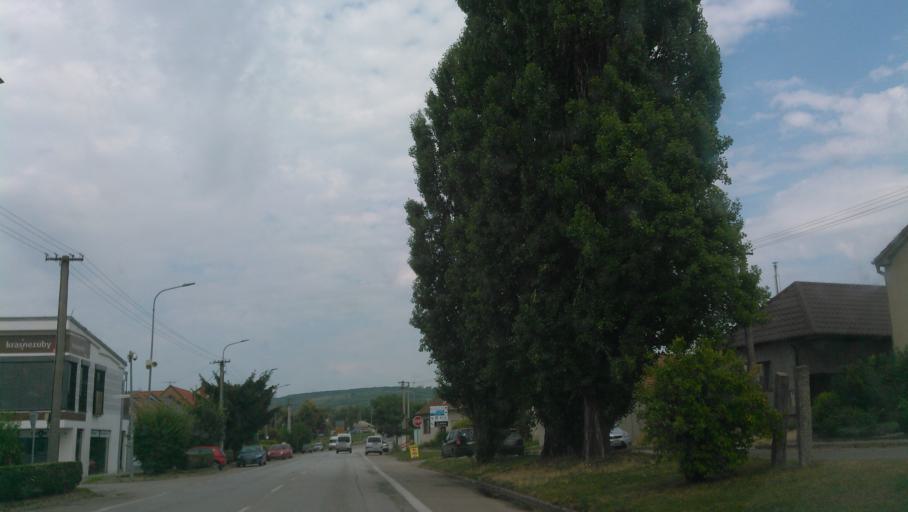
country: SK
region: Trnavsky
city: Hlohovec
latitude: 48.4336
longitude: 17.8018
